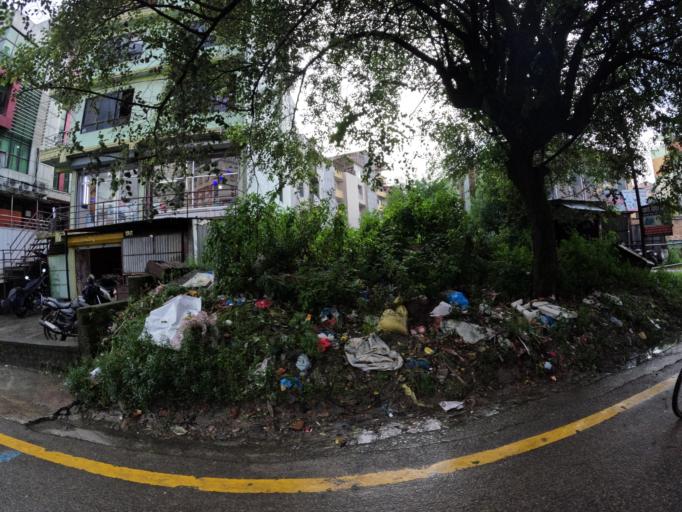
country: NP
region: Central Region
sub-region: Bagmati Zone
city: Kathmandu
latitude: 27.7517
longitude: 85.3261
